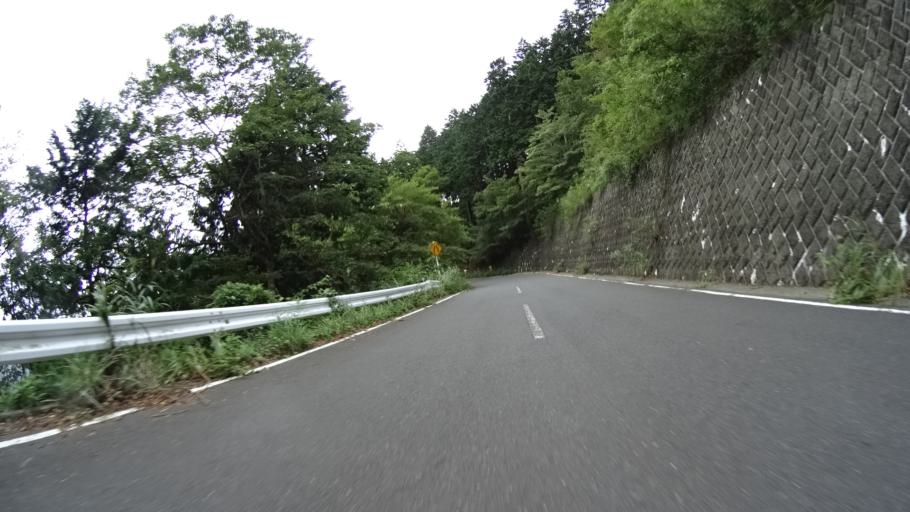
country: JP
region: Kanagawa
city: Hadano
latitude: 35.4181
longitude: 139.2143
